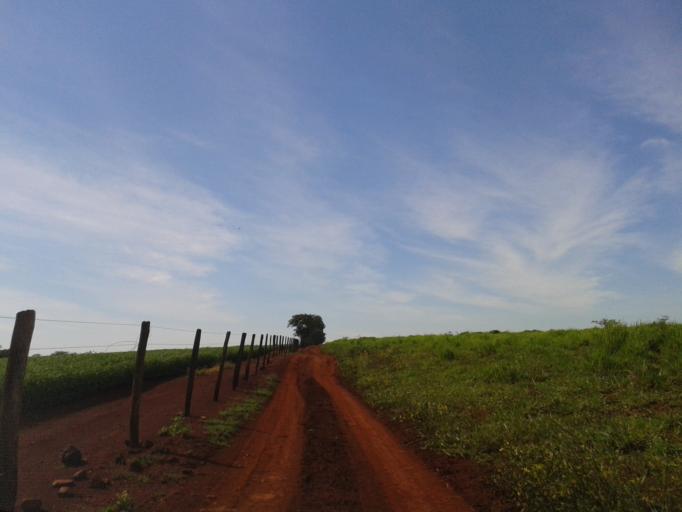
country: BR
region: Minas Gerais
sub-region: Capinopolis
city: Capinopolis
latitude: -18.6271
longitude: -49.7345
